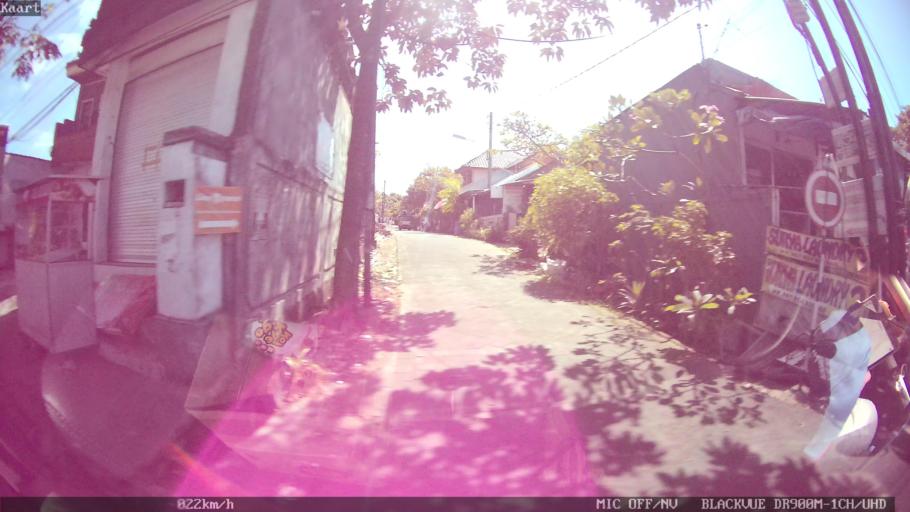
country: ID
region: Bali
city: Banjar Kertasari
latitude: -8.6247
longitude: 115.1821
